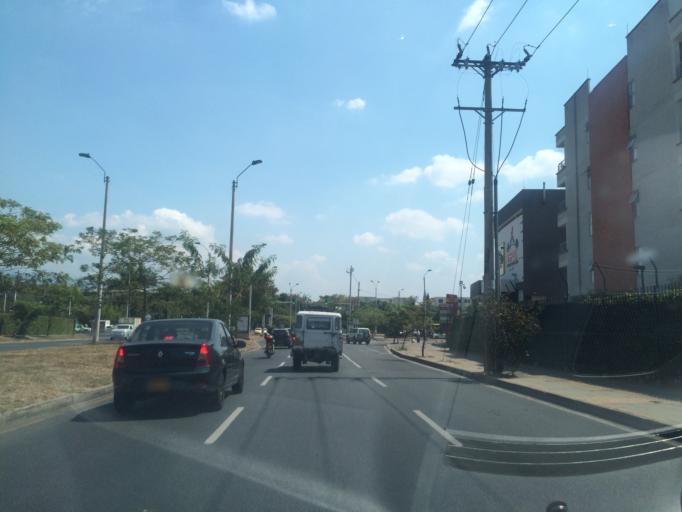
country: CO
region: Valle del Cauca
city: Cali
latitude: 3.3964
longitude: -76.5279
